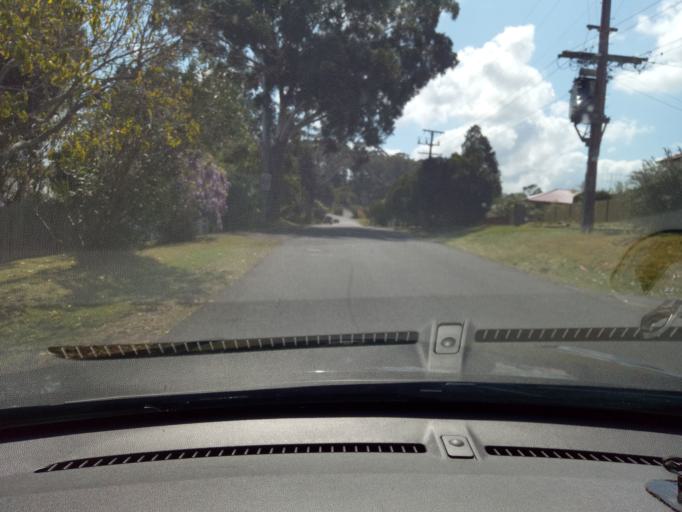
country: AU
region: New South Wales
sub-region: Gosford Shire
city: Narara
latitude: -33.4006
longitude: 151.3505
